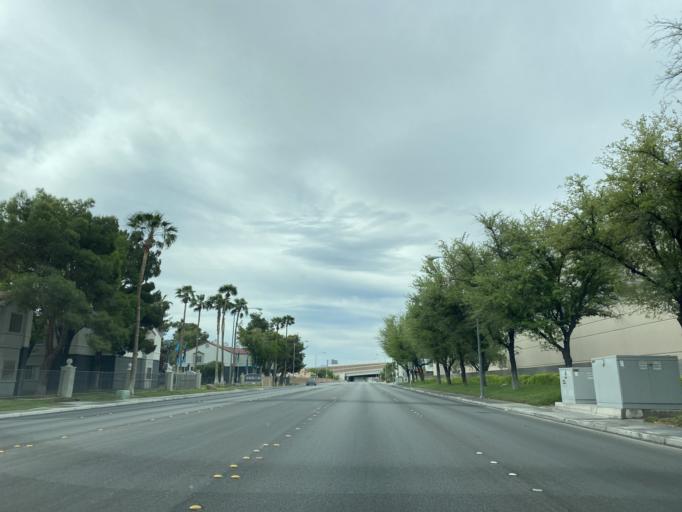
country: US
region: Nevada
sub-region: Clark County
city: Paradise
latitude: 36.0624
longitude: -115.1412
